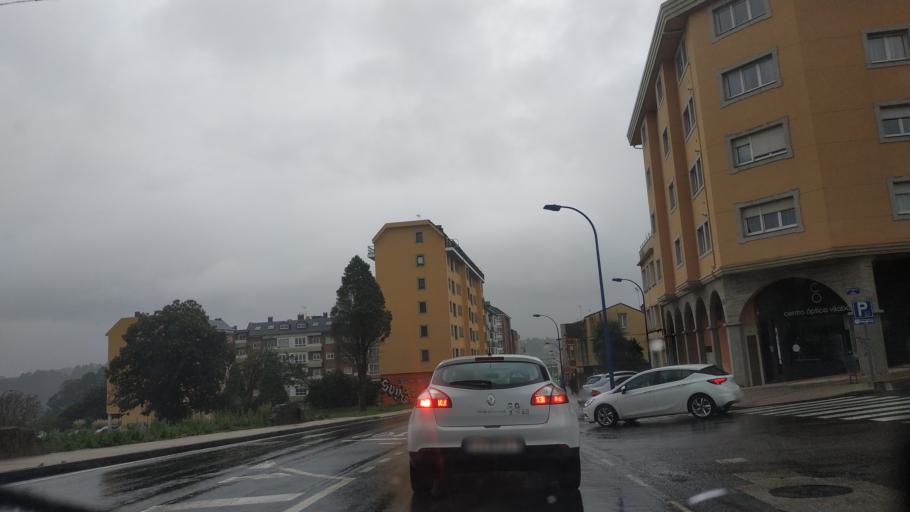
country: ES
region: Galicia
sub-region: Provincia da Coruna
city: Culleredo
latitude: 43.3171
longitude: -8.3837
